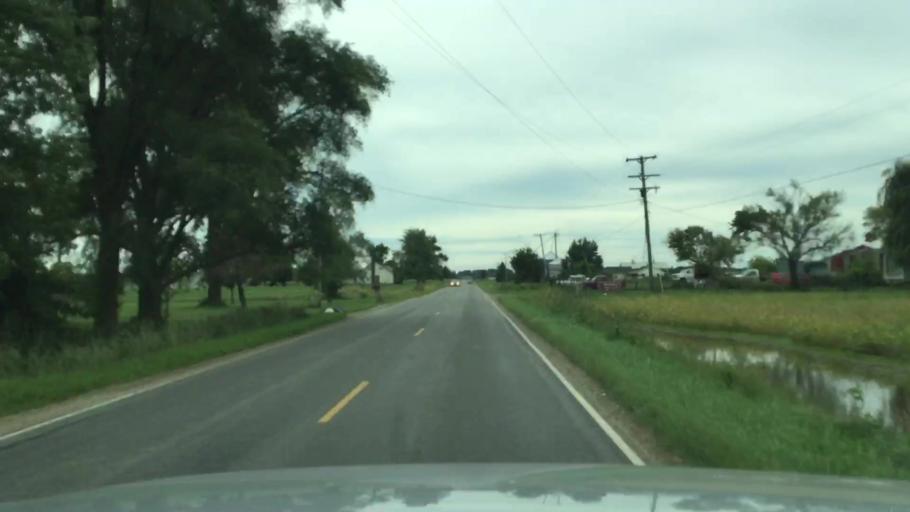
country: US
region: Michigan
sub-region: Shiawassee County
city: Durand
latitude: 43.0110
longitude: -83.9871
